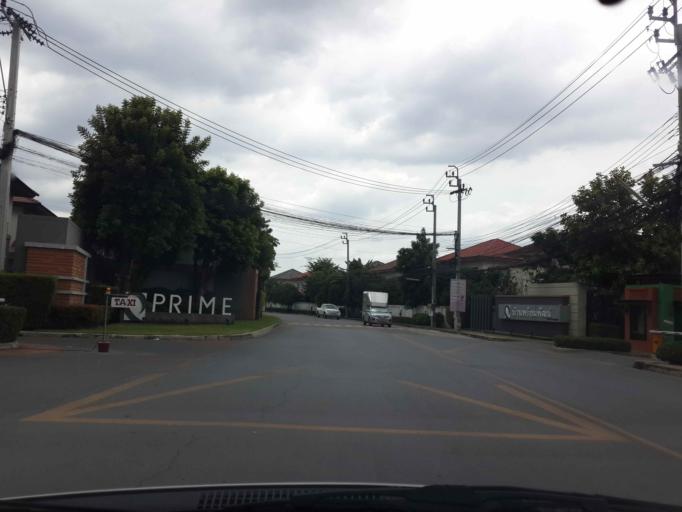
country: TH
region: Bangkok
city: Khlong Sam Wa
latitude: 13.8809
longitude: 100.7114
